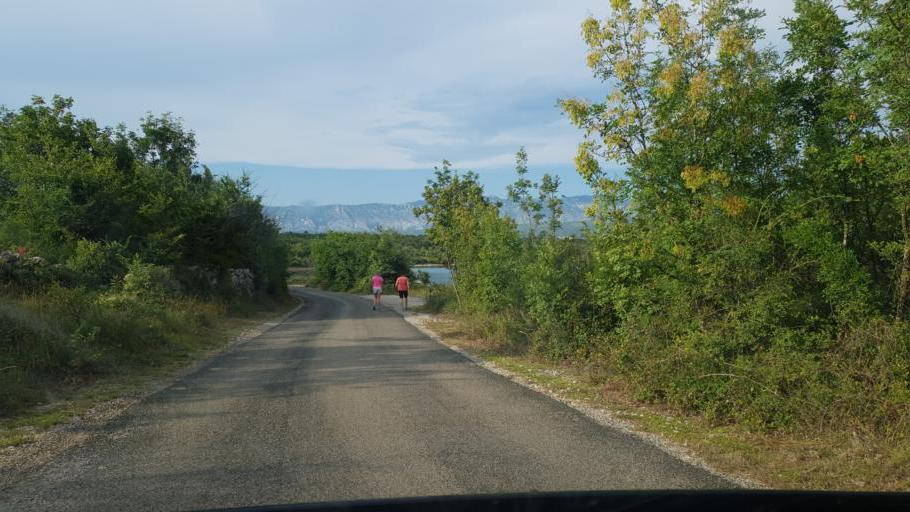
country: HR
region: Primorsko-Goranska
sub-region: Grad Crikvenica
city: Jadranovo
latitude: 45.1683
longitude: 14.6062
